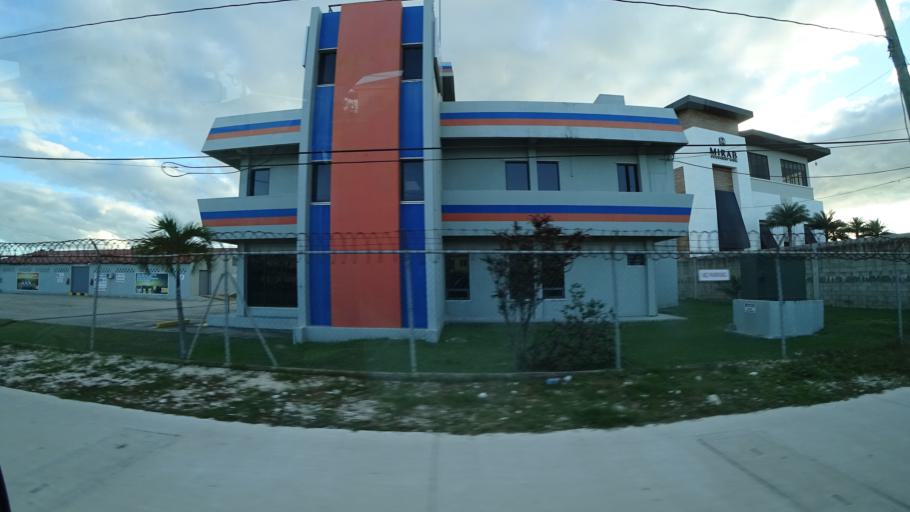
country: BZ
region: Belize
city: Belize City
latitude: 17.5108
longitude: -88.2130
